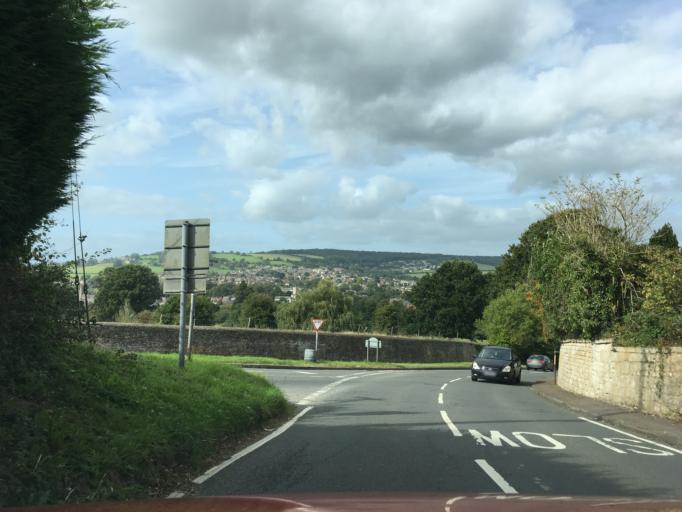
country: GB
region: England
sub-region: Gloucestershire
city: Stroud
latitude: 51.7350
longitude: -2.2412
